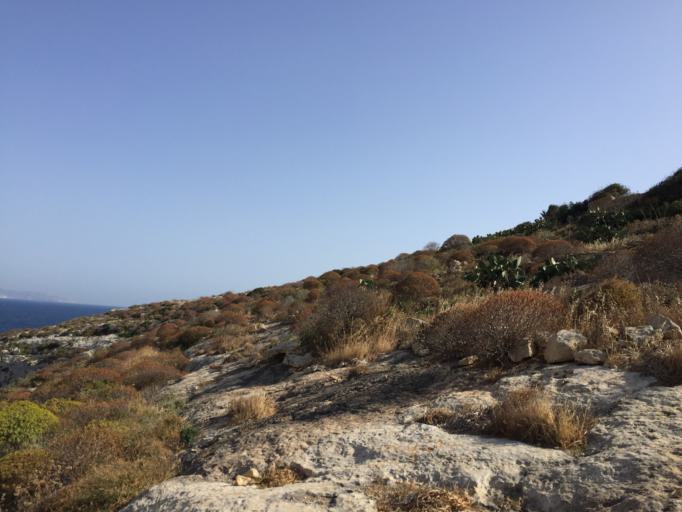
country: MT
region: Ghajnsielem
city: Ghajnsielem
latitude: 36.0189
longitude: 14.2719
